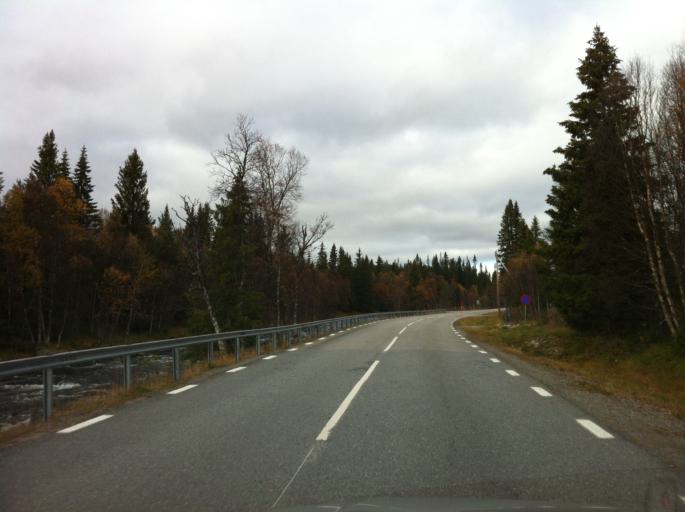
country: NO
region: Hedmark
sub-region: Engerdal
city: Engerdal
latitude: 62.0728
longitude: 12.3105
